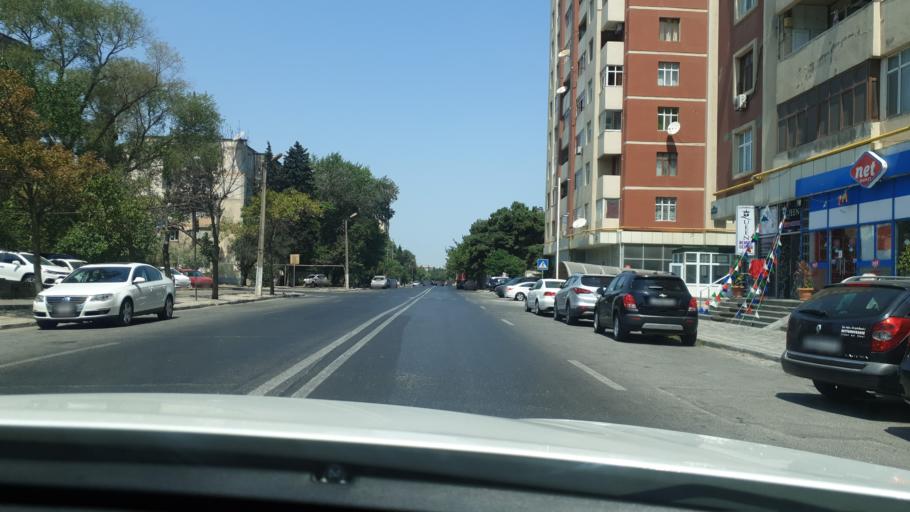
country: AZ
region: Baki
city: Bakixanov
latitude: 40.4147
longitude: 49.9483
